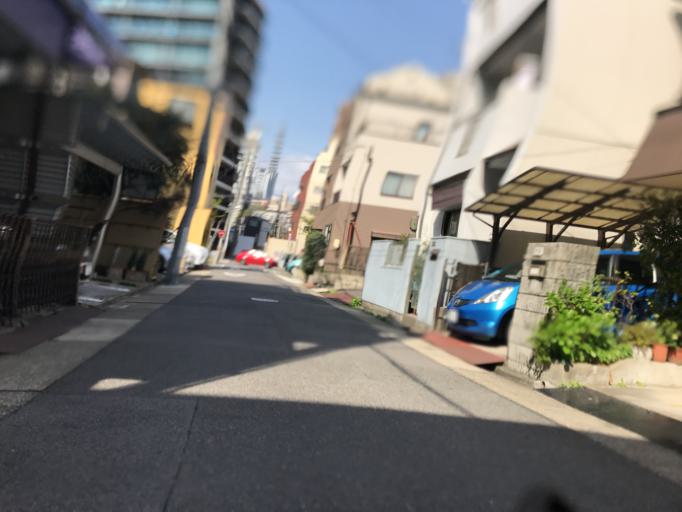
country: JP
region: Aichi
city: Nagoya-shi
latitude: 35.1774
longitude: 136.9184
